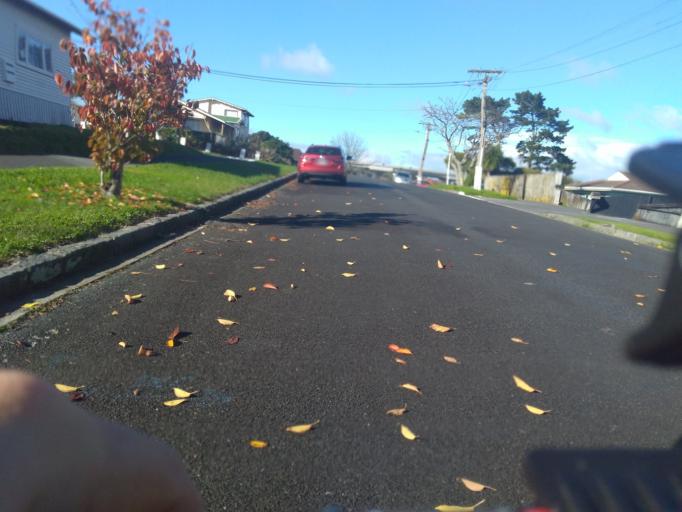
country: NZ
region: Auckland
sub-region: Auckland
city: Rosebank
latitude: -36.8696
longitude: 174.7032
